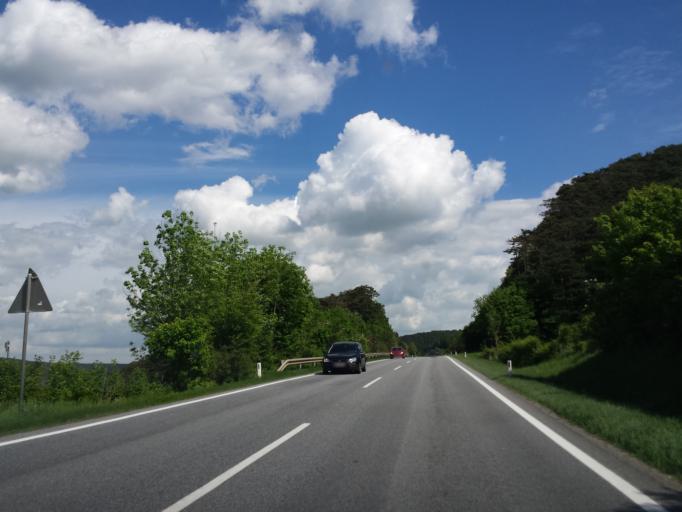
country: AT
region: Lower Austria
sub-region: Politischer Bezirk Wiener Neustadt
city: Markt Piesting
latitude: 47.8705
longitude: 16.1041
